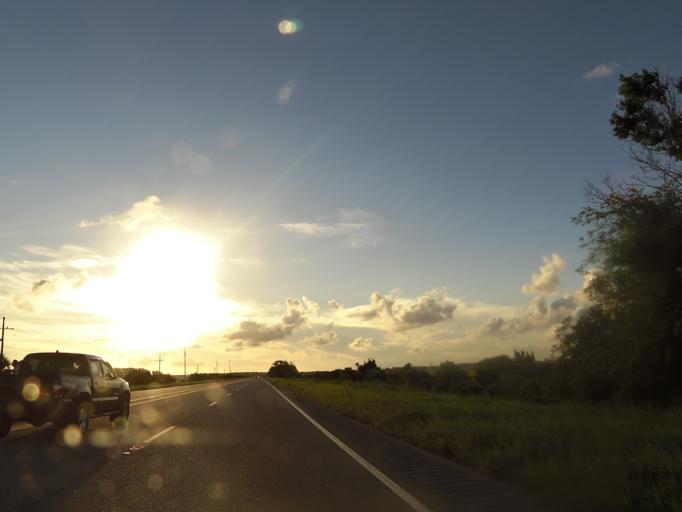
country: US
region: Georgia
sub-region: Glynn County
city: Brunswick
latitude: 31.1085
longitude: -81.5104
